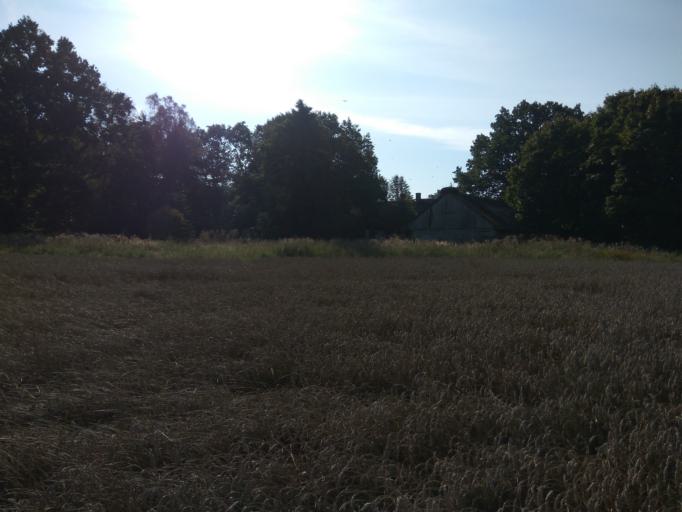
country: LV
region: Ventspils
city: Ventspils
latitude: 57.3568
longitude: 21.6636
